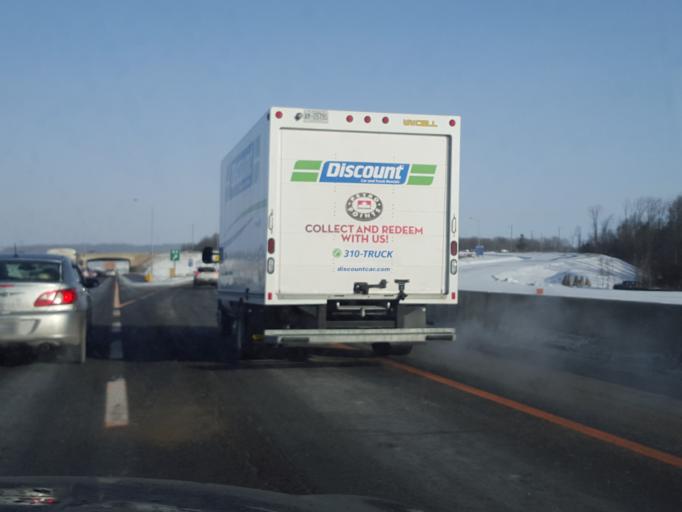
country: CA
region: Ontario
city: Bradford West Gwillimbury
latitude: 44.0262
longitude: -79.5933
